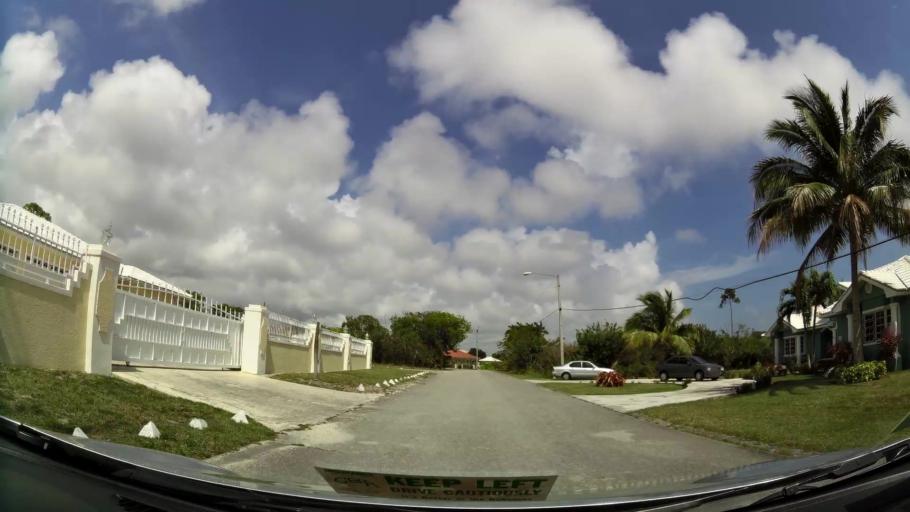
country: BS
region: Freeport
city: Freeport
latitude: 26.5072
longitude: -78.7114
